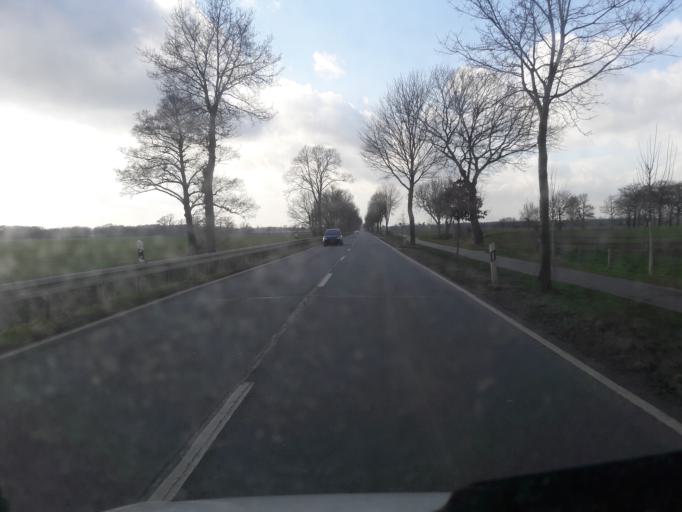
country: DE
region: Lower Saxony
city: Raddestorf
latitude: 52.5006
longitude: 8.9712
